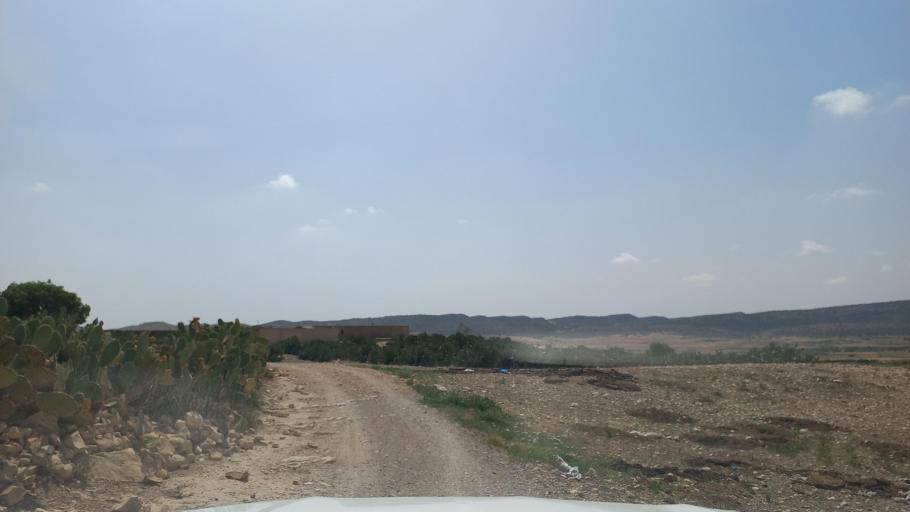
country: TN
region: Al Qasrayn
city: Sbiba
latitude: 35.4058
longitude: 8.9711
